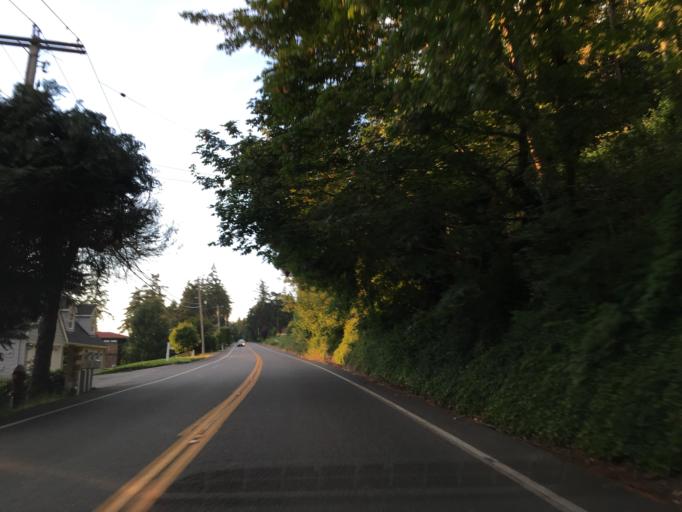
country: US
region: Washington
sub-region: Whatcom County
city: Bellingham
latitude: 48.6875
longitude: -122.4908
